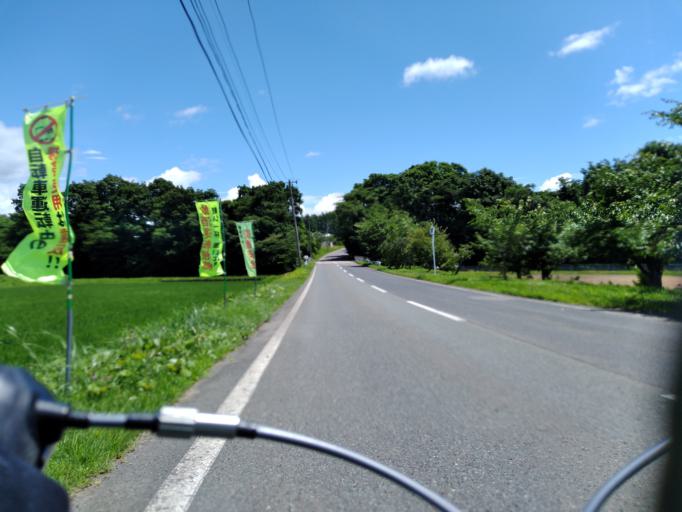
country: JP
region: Iwate
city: Shizukuishi
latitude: 39.7616
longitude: 140.9657
